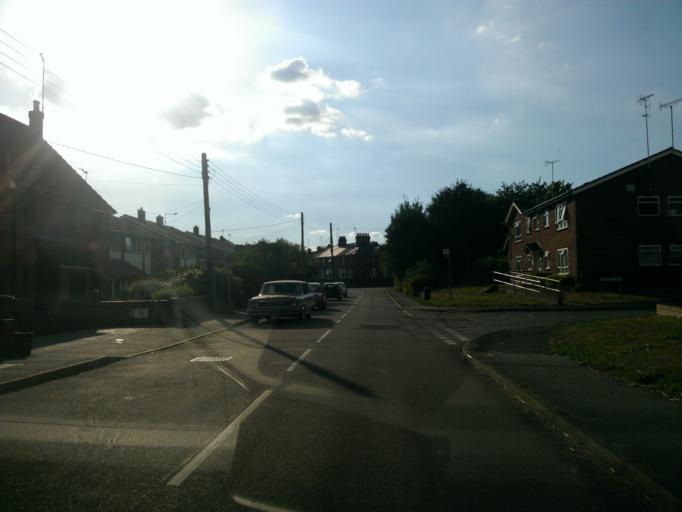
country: GB
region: England
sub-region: Essex
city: Sible Hedingham
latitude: 51.9921
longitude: 0.5961
